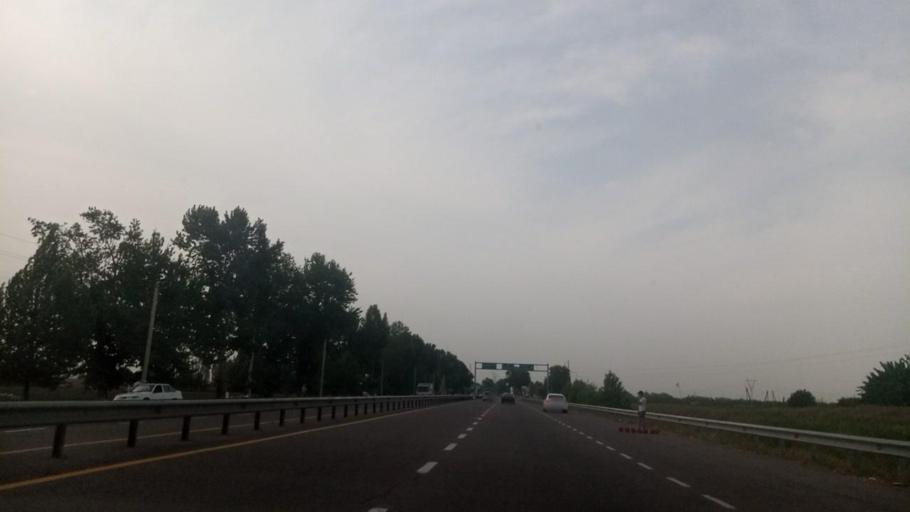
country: UZ
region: Toshkent Shahri
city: Bektemir
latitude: 41.1781
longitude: 69.4090
